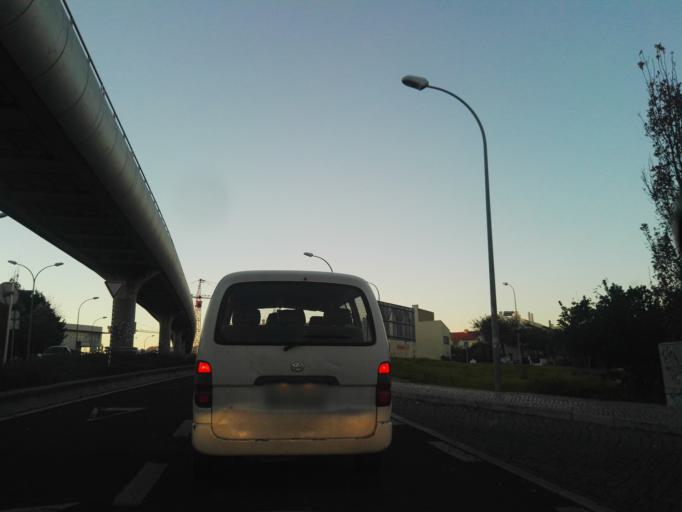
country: PT
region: Lisbon
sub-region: Oeiras
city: Paco de Arcos
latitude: 38.7027
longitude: -9.2991
